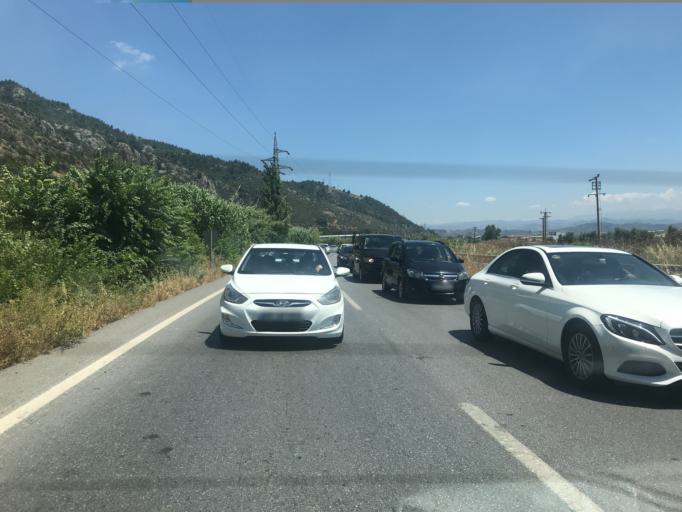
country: TR
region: Aydin
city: Soeke
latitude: 37.7945
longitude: 27.4668
